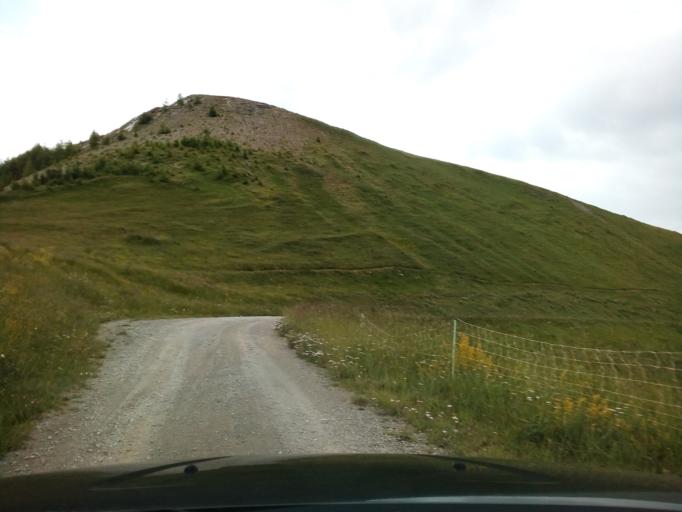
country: FR
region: Rhone-Alpes
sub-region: Departement de l'Isere
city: Mont-de-Lans
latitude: 45.0633
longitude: 6.1844
